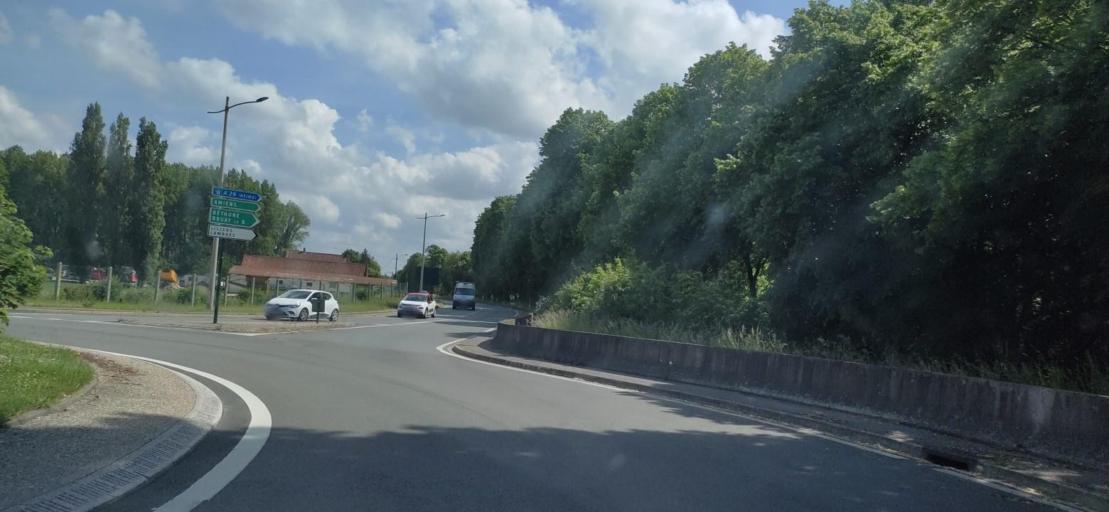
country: FR
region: Nord-Pas-de-Calais
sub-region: Departement du Pas-de-Calais
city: Aire-sur-la-Lys
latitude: 50.6281
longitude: 2.3907
